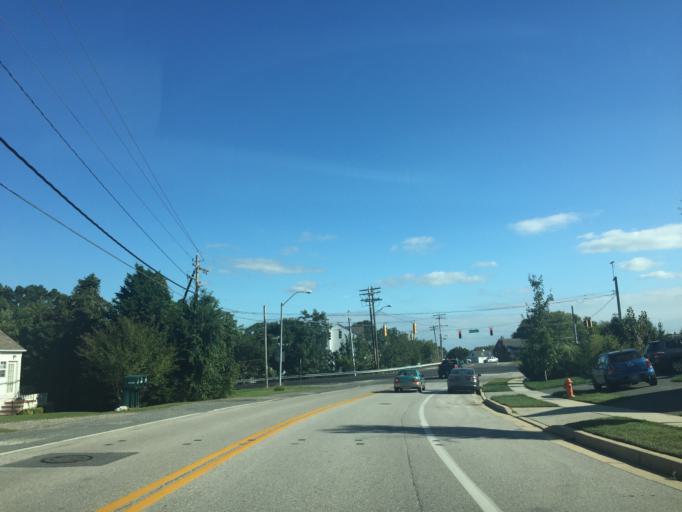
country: US
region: Maryland
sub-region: Baltimore County
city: Rossville
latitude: 39.3644
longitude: -76.4919
